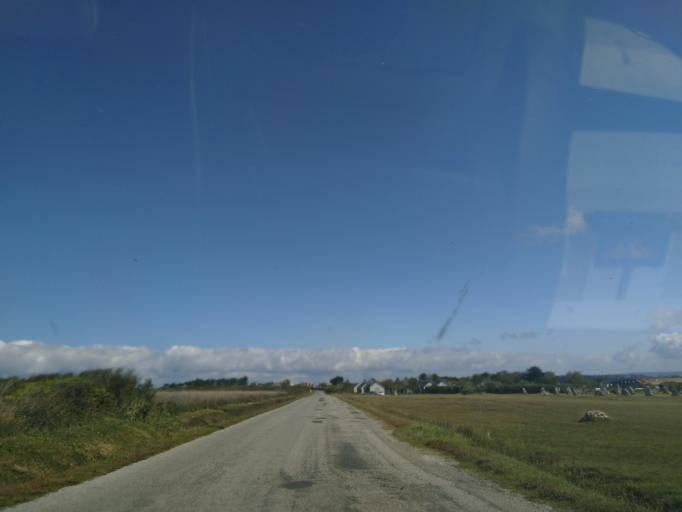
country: FR
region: Brittany
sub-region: Departement du Finistere
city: Camaret-sur-Mer
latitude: 48.2727
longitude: -4.6114
